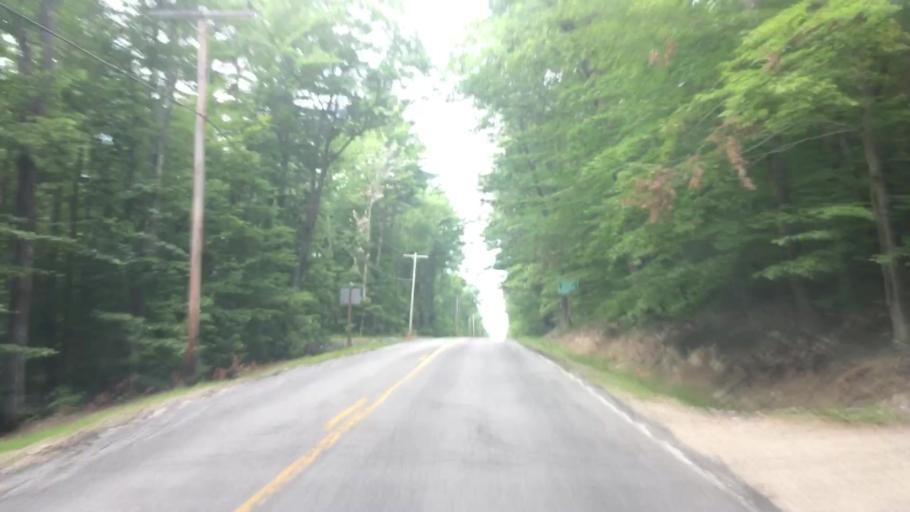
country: US
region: Maine
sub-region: Oxford County
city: Oxford
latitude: 44.0209
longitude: -70.5284
